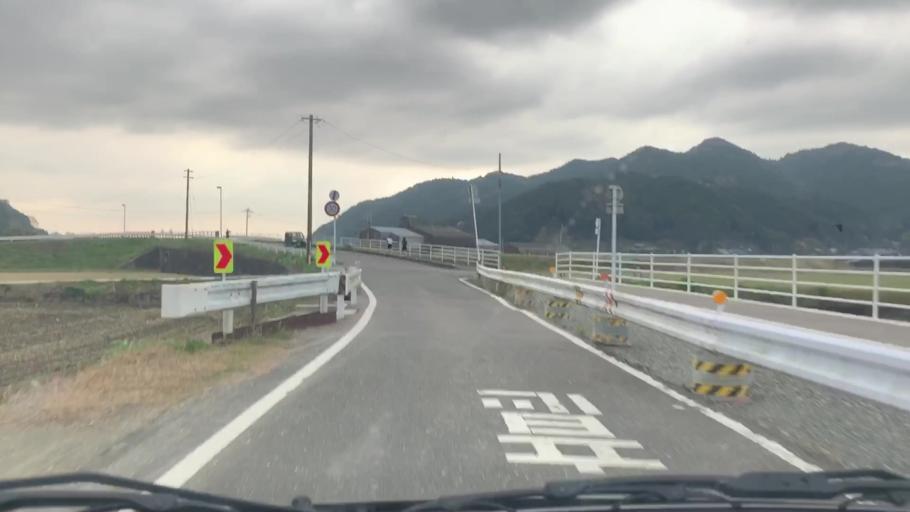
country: JP
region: Saga Prefecture
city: Ureshinomachi-shimojuku
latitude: 33.1263
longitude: 130.0346
